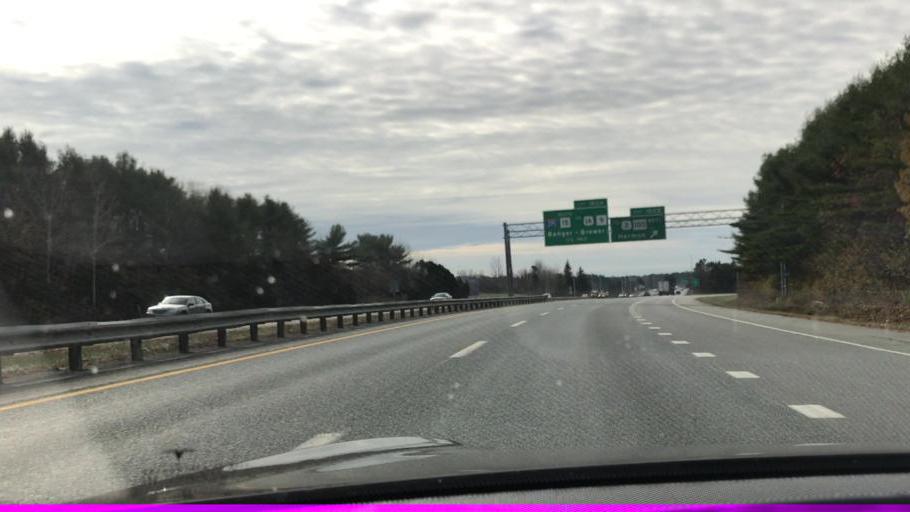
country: US
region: Maine
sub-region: Penobscot County
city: Bangor
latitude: 44.7937
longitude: -68.8038
